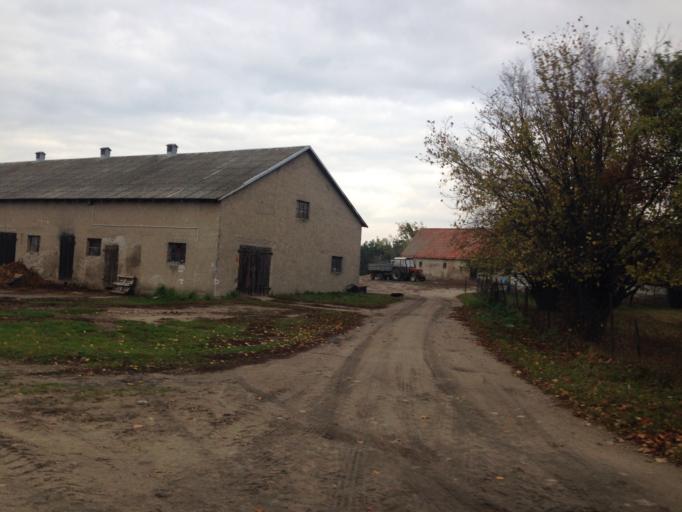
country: PL
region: Kujawsko-Pomorskie
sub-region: Powiat brodnicki
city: Brzozie
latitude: 53.2995
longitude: 19.6047
